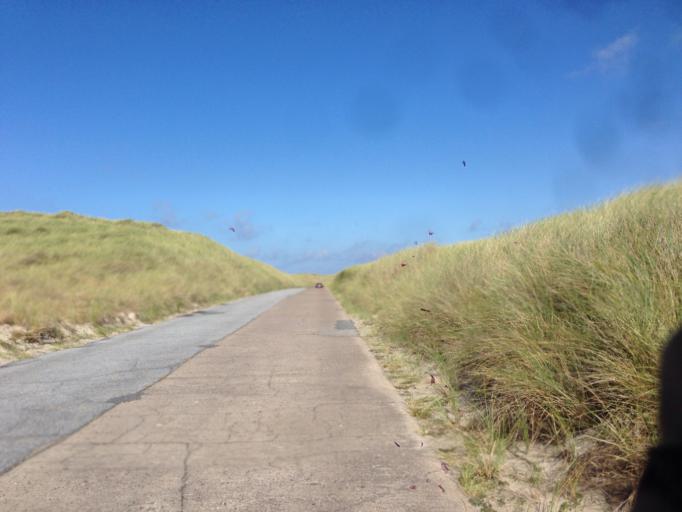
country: DE
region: Schleswig-Holstein
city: List
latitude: 55.0435
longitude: 8.3916
